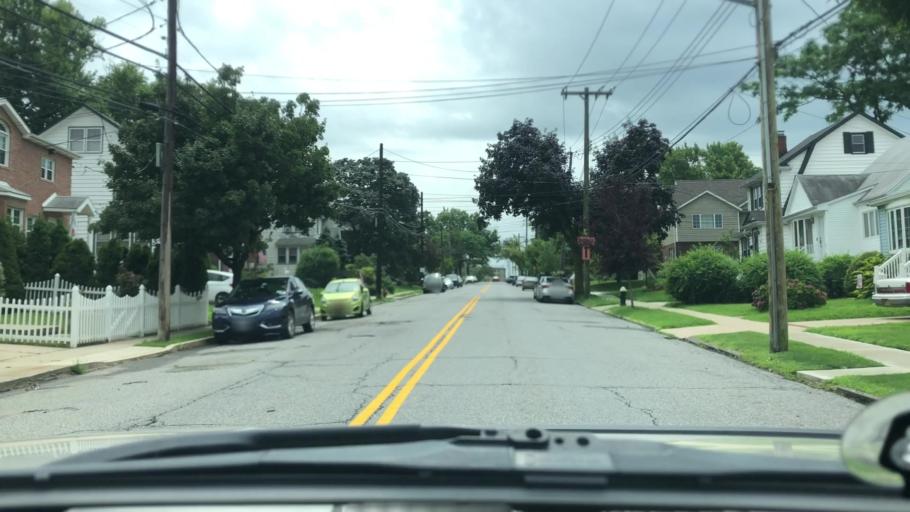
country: US
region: New Jersey
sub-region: Hudson County
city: Bayonne
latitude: 40.6251
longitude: -74.1107
